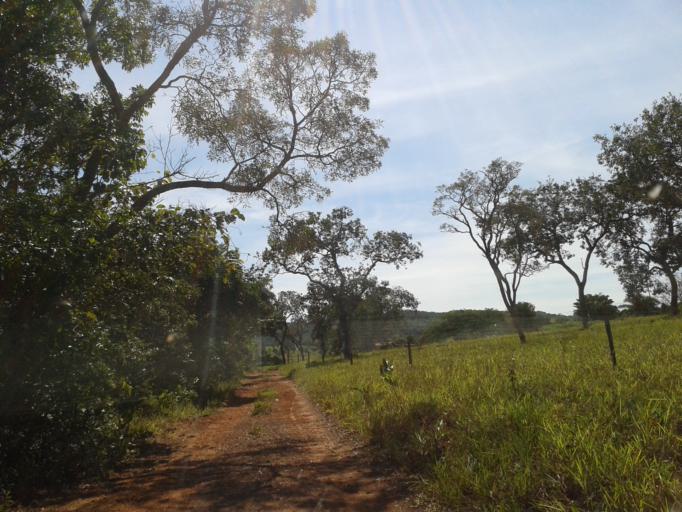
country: BR
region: Minas Gerais
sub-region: Campina Verde
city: Campina Verde
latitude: -19.4365
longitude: -49.6921
